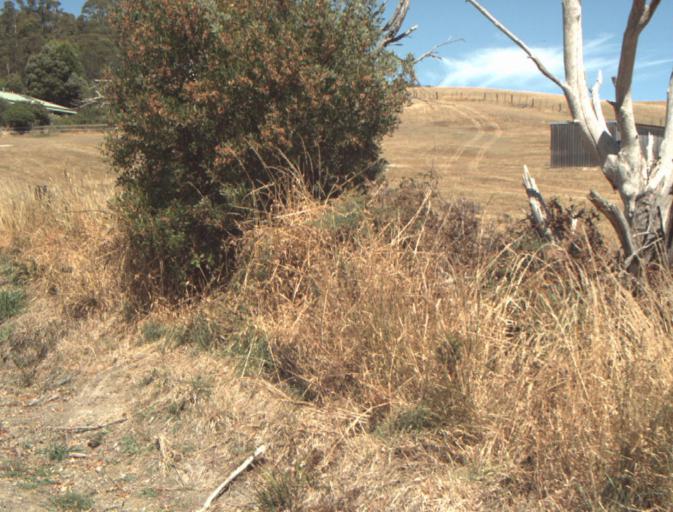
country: AU
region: Tasmania
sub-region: Launceston
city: Mayfield
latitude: -41.2645
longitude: 147.1492
